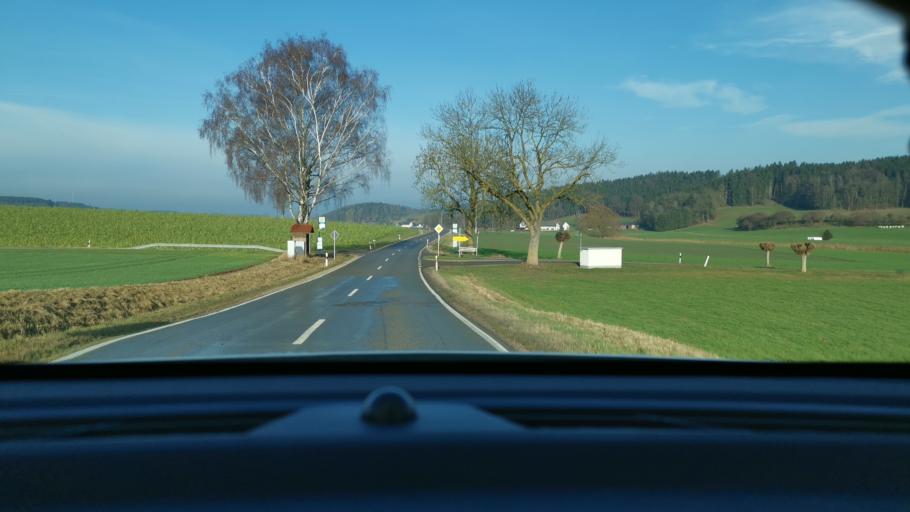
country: DE
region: Bavaria
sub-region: Swabia
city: Aindling
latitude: 48.5657
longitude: 10.9799
